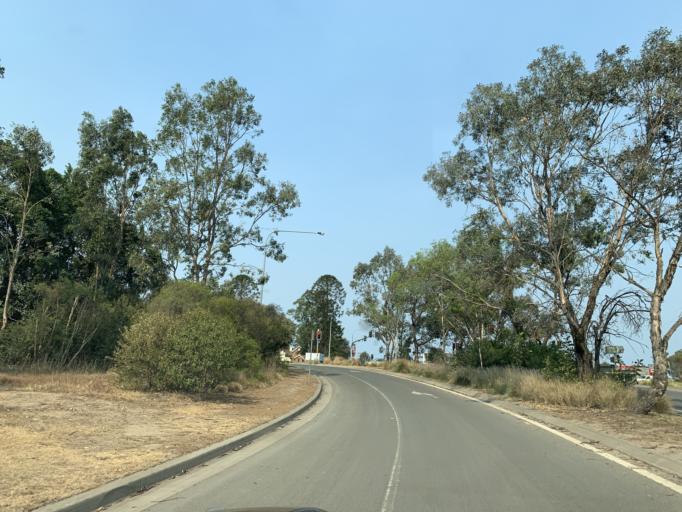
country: AU
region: New South Wales
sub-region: Blacktown
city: Rouse Hill
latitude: -33.6842
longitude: 150.9158
